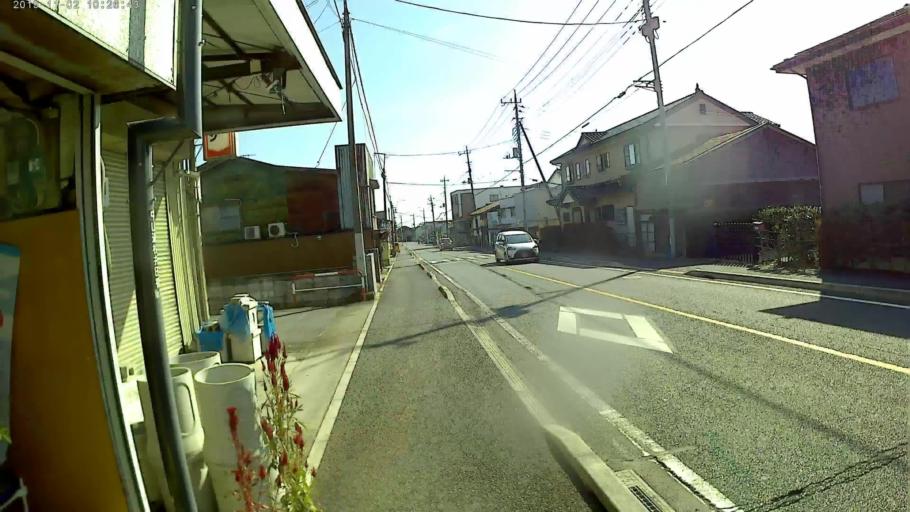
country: JP
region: Gunma
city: Annaka
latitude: 36.3127
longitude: 138.8025
